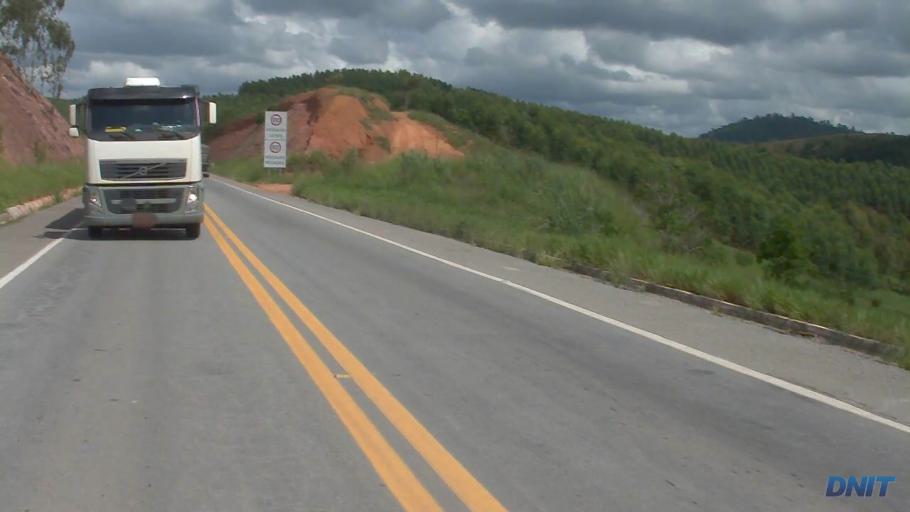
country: BR
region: Minas Gerais
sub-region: Governador Valadares
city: Governador Valadares
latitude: -19.0698
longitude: -42.1750
